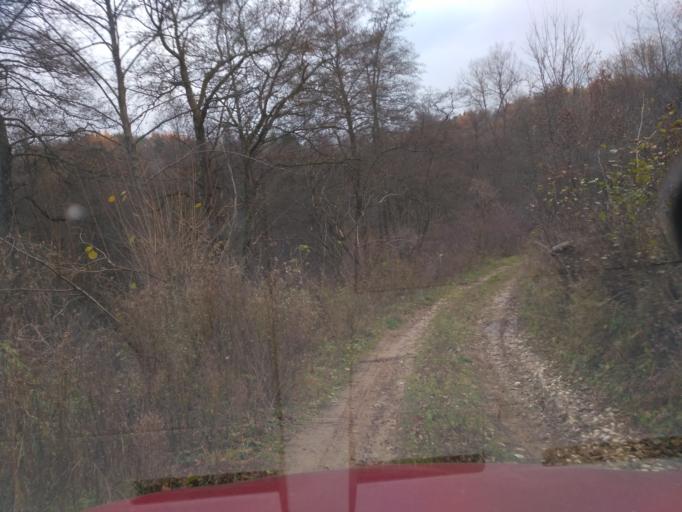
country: SK
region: Presovsky
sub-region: Okres Presov
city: Presov
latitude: 48.9322
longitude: 21.2115
